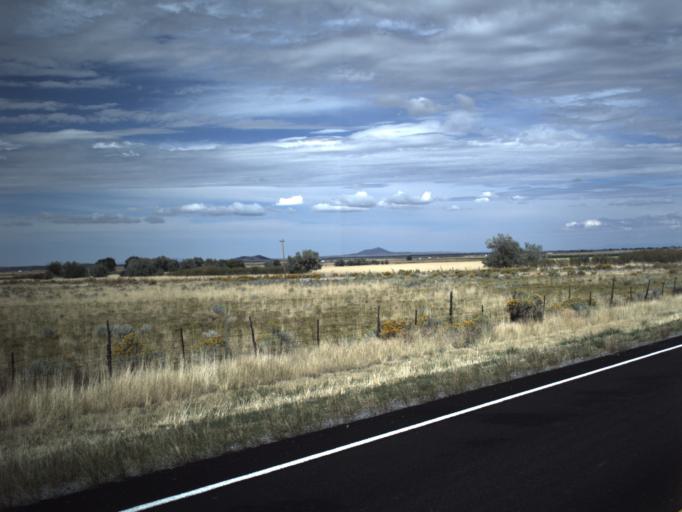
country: US
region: Utah
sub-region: Millard County
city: Fillmore
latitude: 38.8387
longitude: -112.4270
